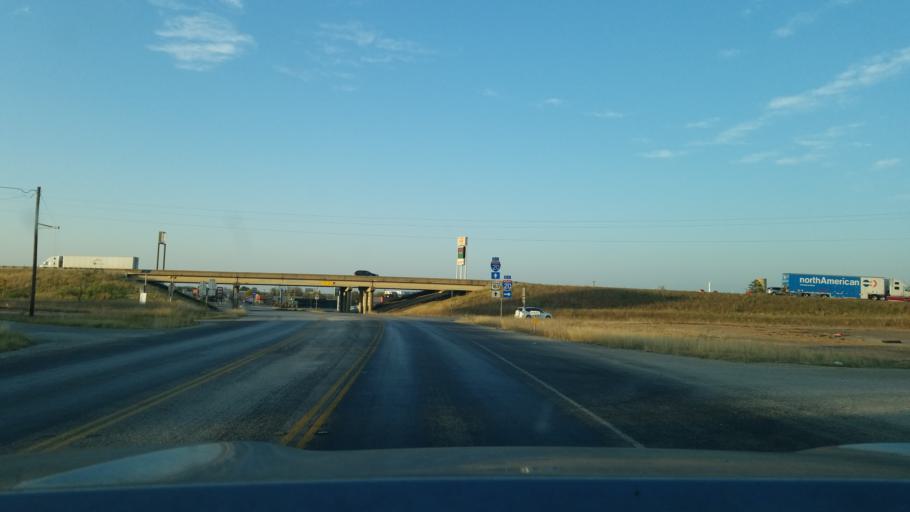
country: US
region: Texas
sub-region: Eastland County
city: Cisco
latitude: 32.3733
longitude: -98.9704
